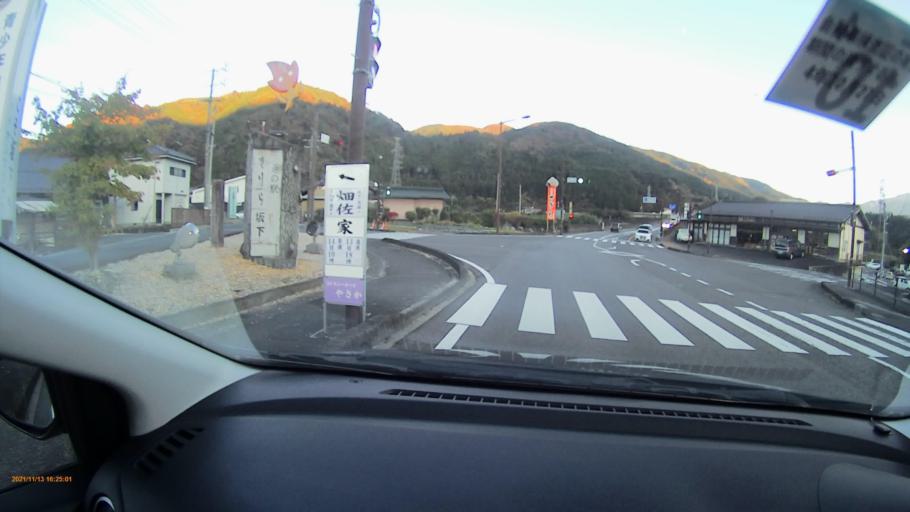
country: JP
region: Gifu
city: Nakatsugawa
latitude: 35.5720
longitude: 137.5344
